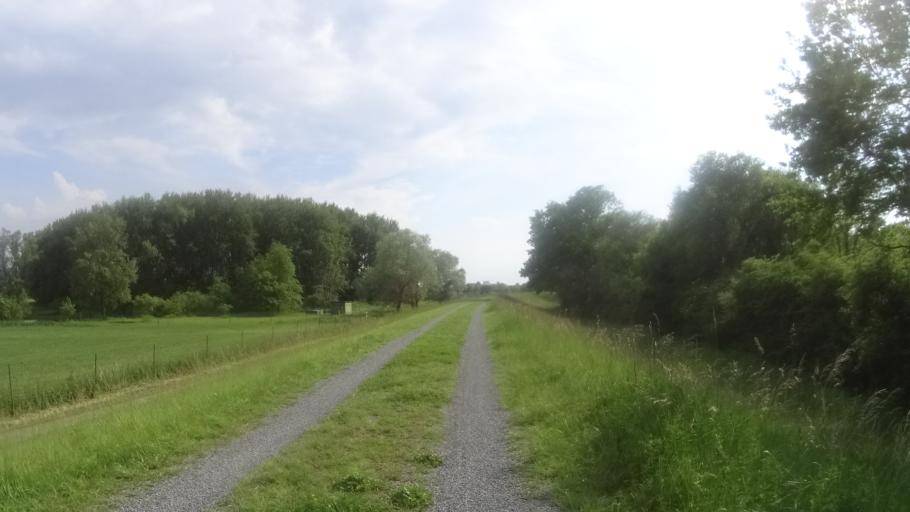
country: DE
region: Baden-Wuerttemberg
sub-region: Karlsruhe Region
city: Hugelsheim
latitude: 48.8082
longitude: 8.1141
